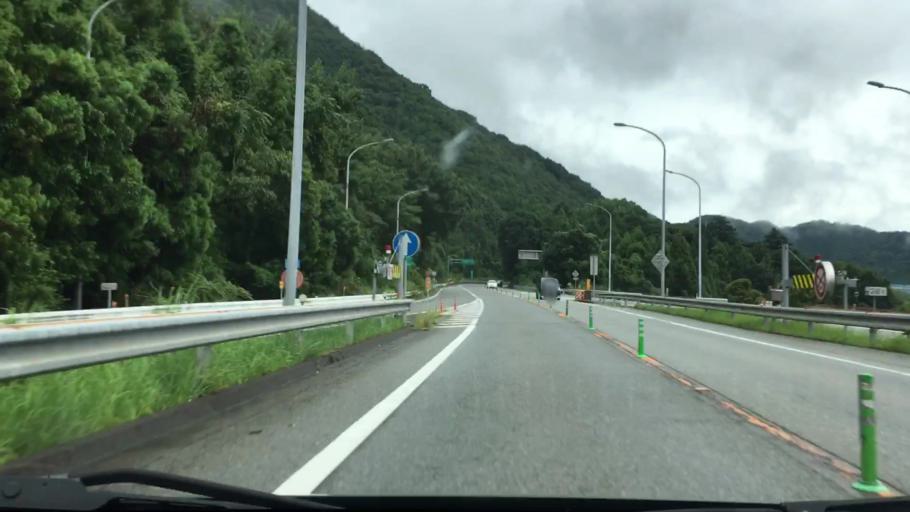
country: JP
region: Hyogo
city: Nishiwaki
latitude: 35.0297
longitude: 134.7661
